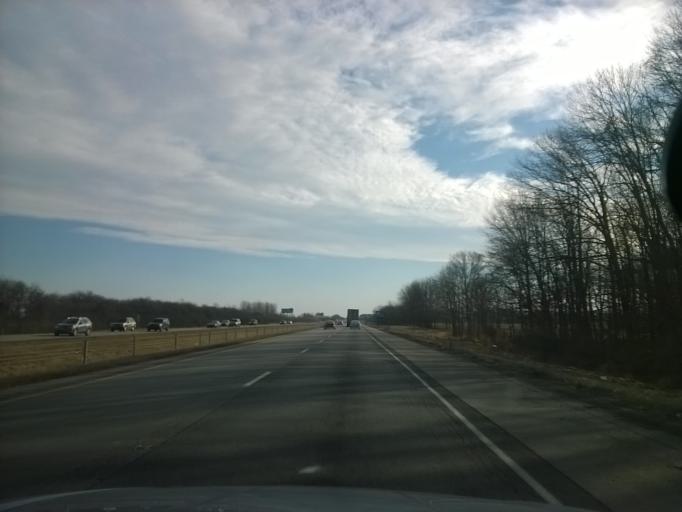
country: US
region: Indiana
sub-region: Johnson County
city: Franklin
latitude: 39.5110
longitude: -86.0219
